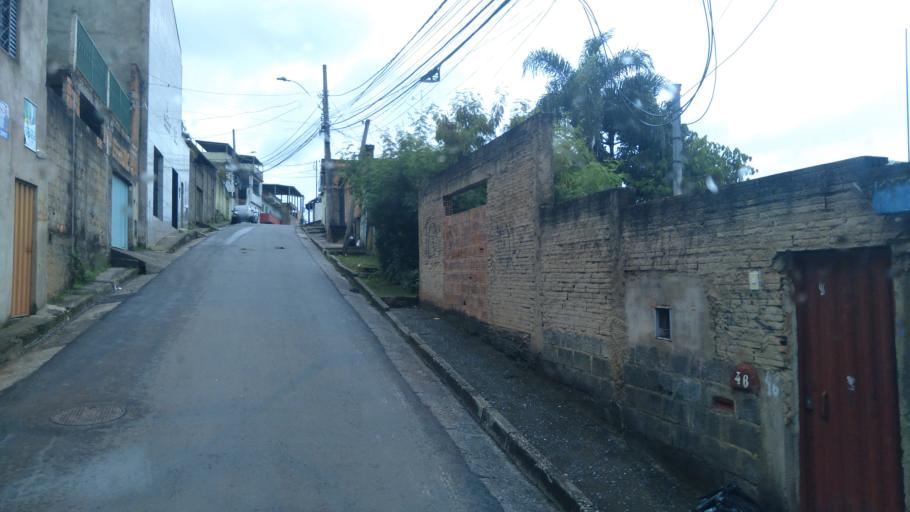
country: BR
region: Minas Gerais
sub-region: Belo Horizonte
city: Belo Horizonte
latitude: -19.9180
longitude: -43.8840
